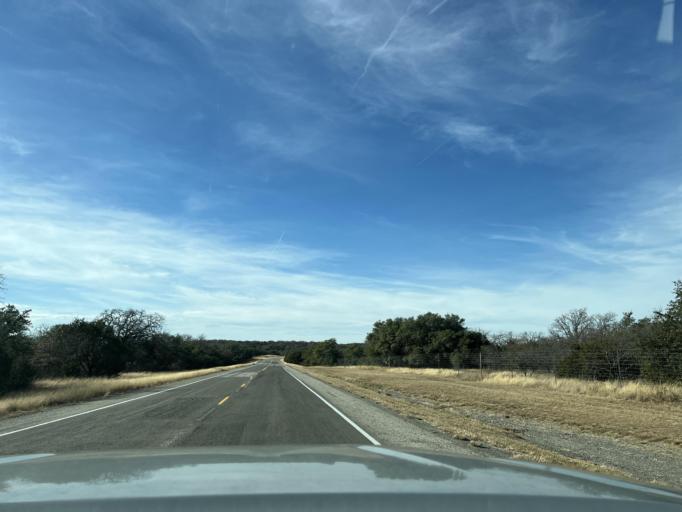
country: US
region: Texas
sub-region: Eastland County
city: Cisco
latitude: 32.4604
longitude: -99.0062
